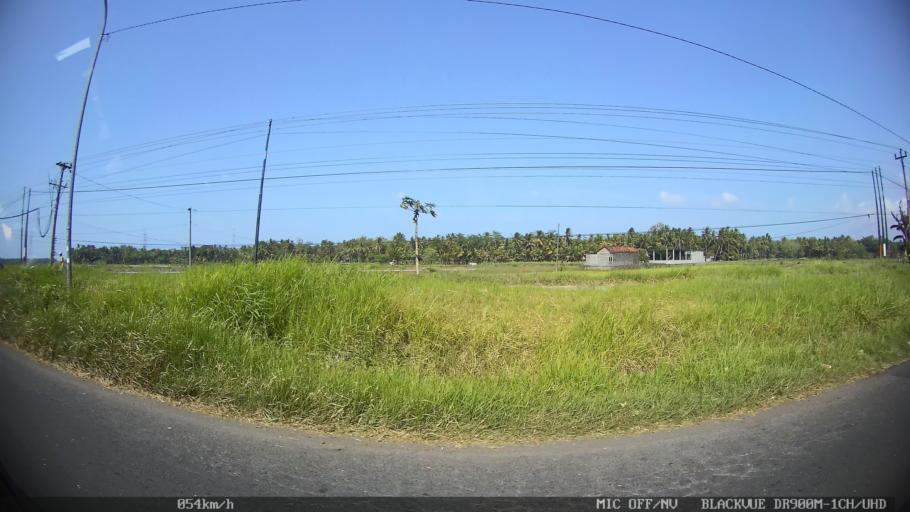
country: ID
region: Daerah Istimewa Yogyakarta
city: Srandakan
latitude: -7.9110
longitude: 110.1755
